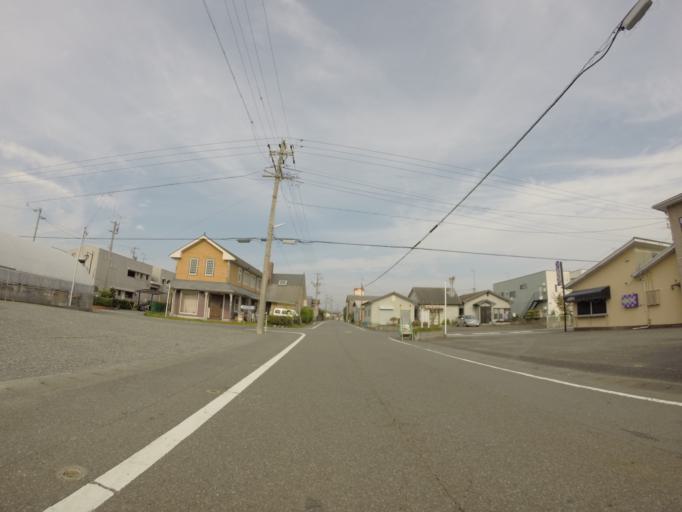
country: JP
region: Shizuoka
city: Sagara
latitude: 34.7312
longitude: 138.2272
